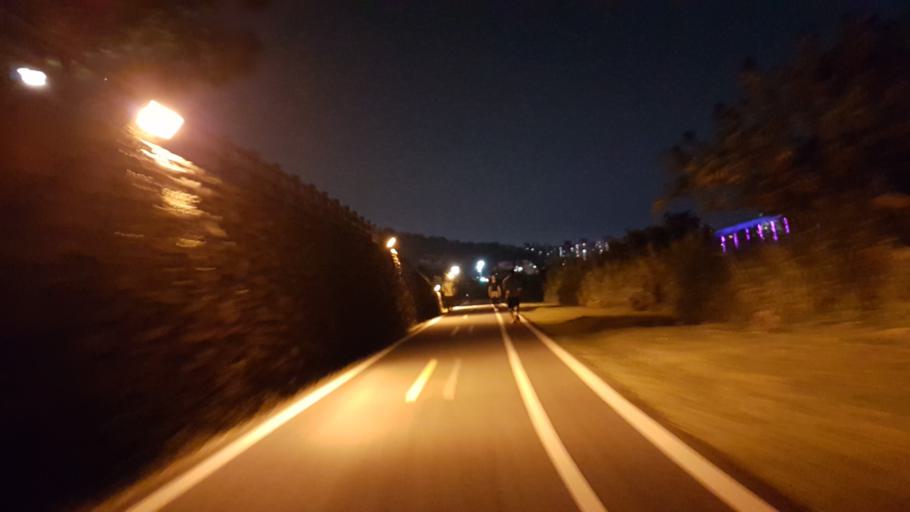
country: TW
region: Taipei
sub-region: Taipei
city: Banqiao
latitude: 24.9747
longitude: 121.5227
